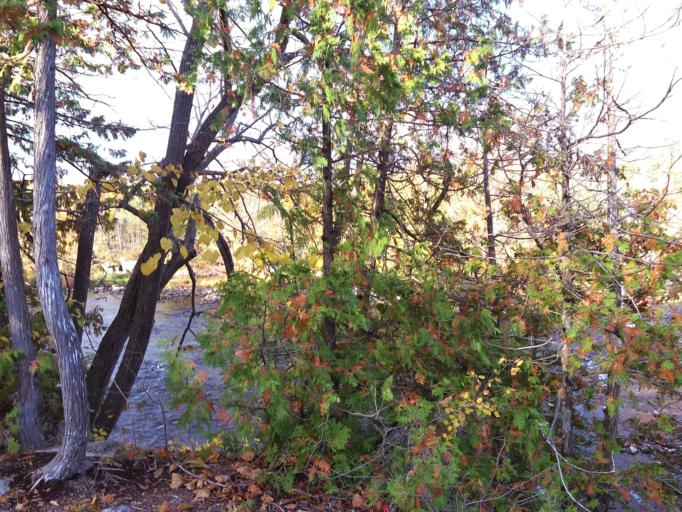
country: CA
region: Ontario
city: Pembroke
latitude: 45.5346
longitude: -77.0922
